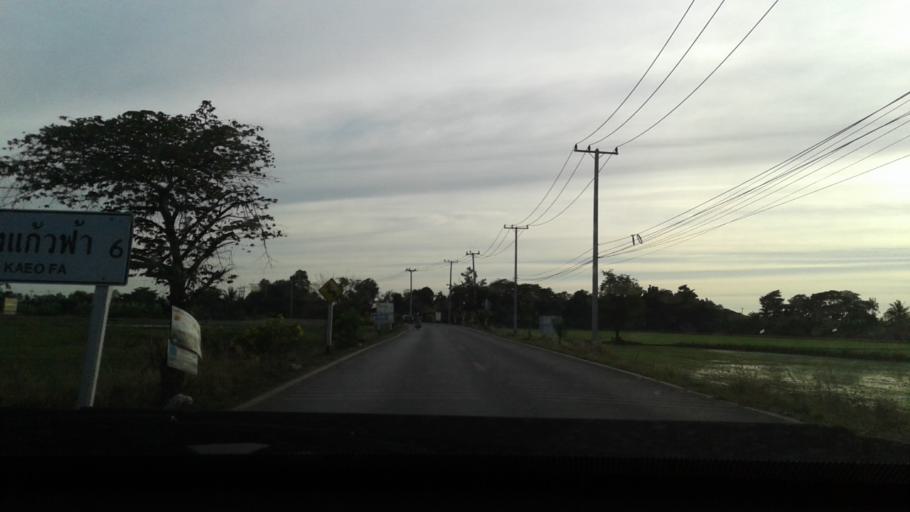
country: TH
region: Nonthaburi
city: Sai Noi
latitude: 13.9222
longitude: 100.2550
